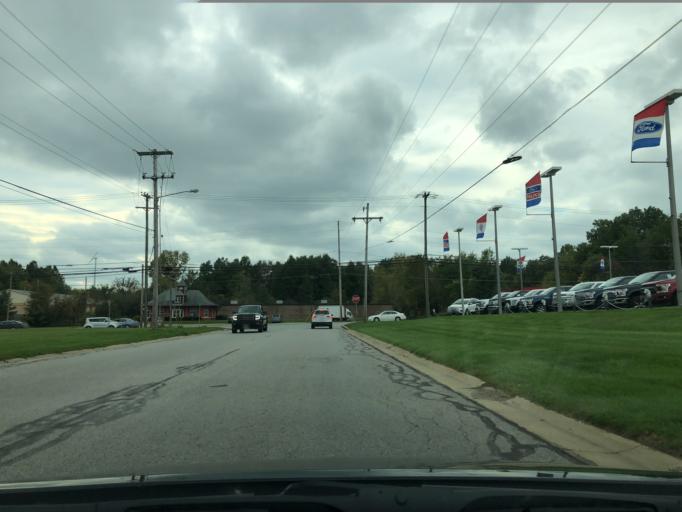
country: US
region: Ohio
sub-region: Summit County
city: Cuyahoga Falls
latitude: 41.1709
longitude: -81.5075
